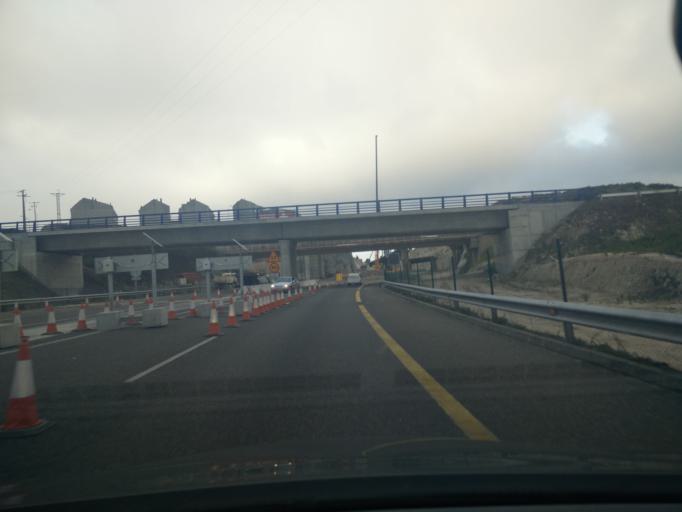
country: ES
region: Galicia
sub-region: Provincia da Coruna
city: Arteixo
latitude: 43.3287
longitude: -8.4596
